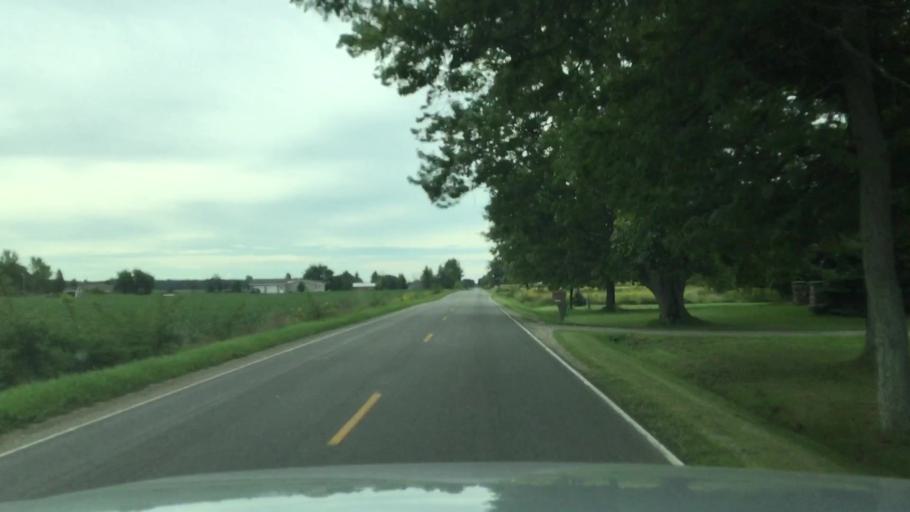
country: US
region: Michigan
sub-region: Shiawassee County
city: Durand
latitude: 43.0422
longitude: -83.9873
